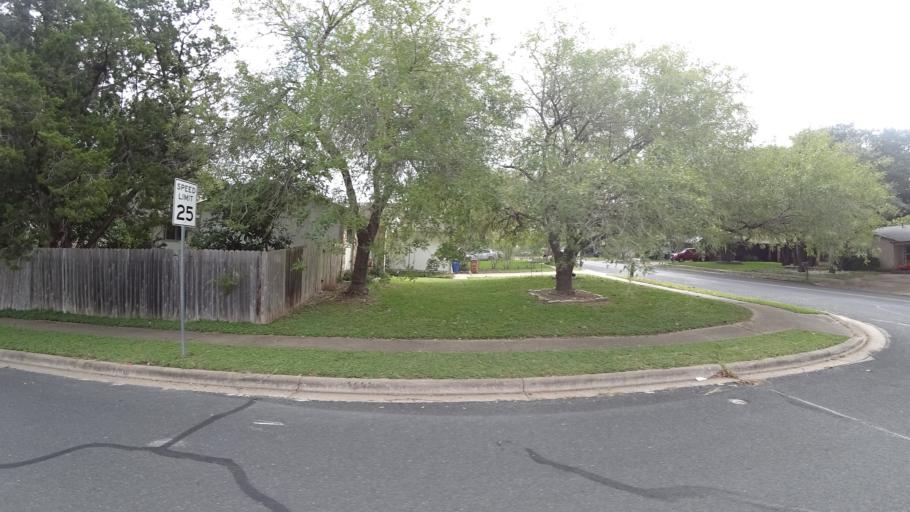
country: US
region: Texas
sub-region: Travis County
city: Shady Hollow
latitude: 30.2044
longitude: -97.8293
